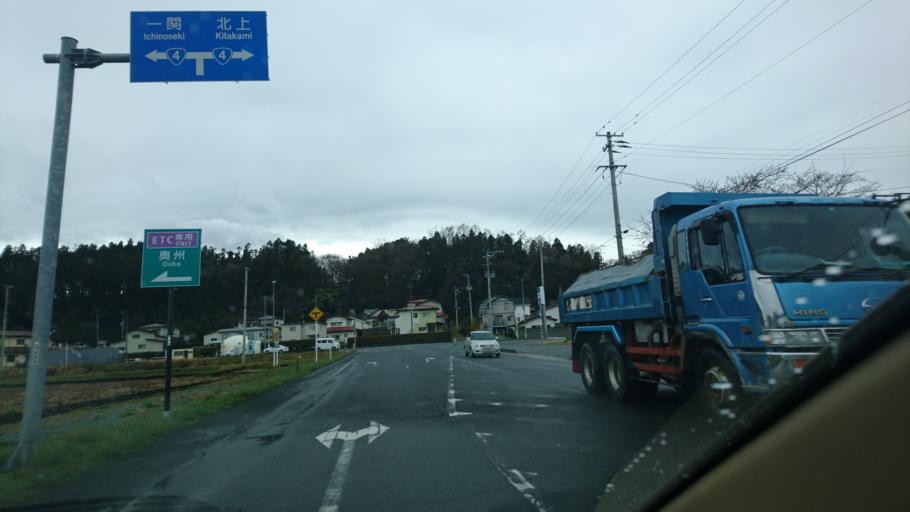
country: JP
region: Iwate
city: Mizusawa
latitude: 39.1005
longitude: 141.1368
